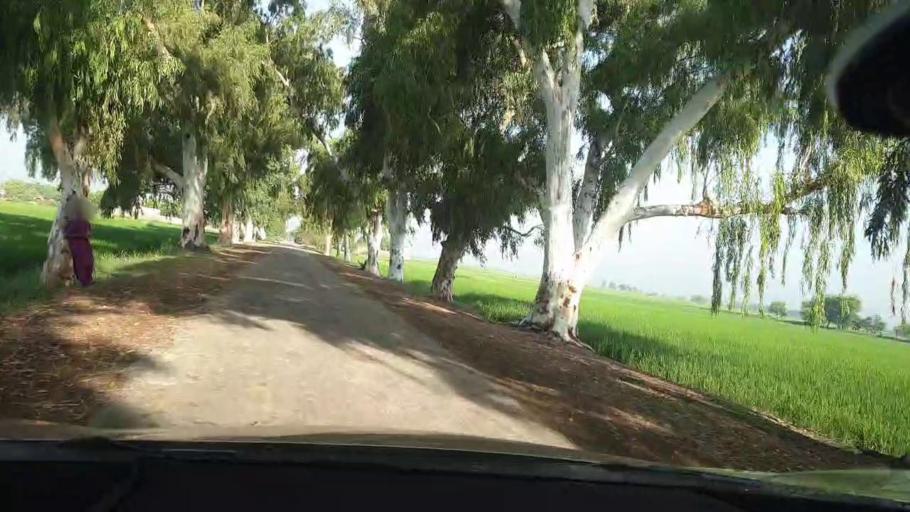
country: PK
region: Sindh
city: Kambar
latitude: 27.6525
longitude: 68.0365
